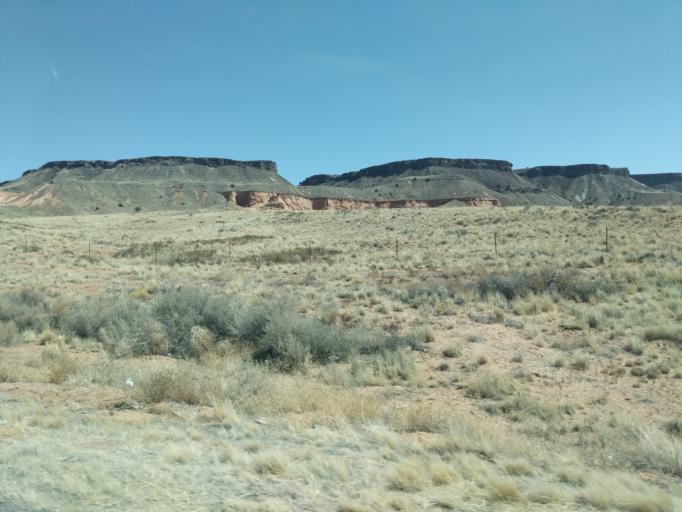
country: US
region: Arizona
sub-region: Navajo County
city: Dilkon
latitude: 35.4323
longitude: -110.0657
